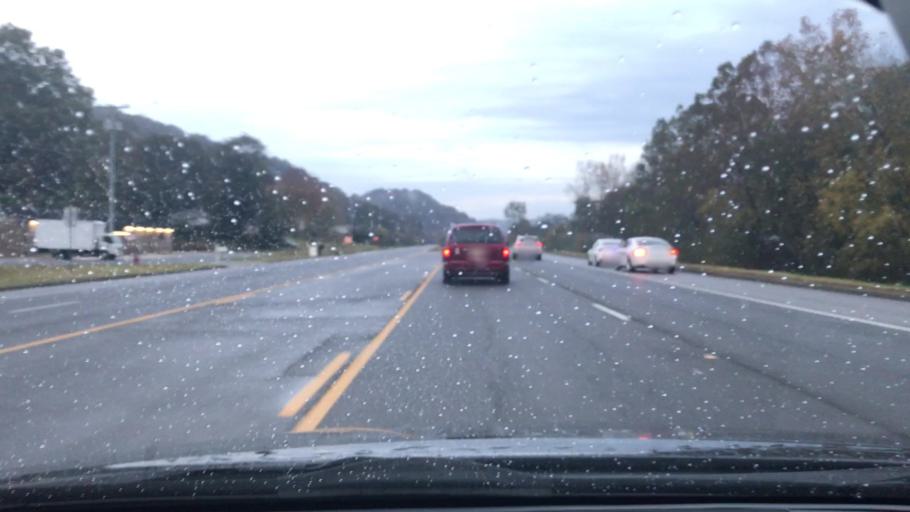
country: US
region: Tennessee
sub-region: Cheatham County
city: Ashland City
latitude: 36.2587
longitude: -87.0436
